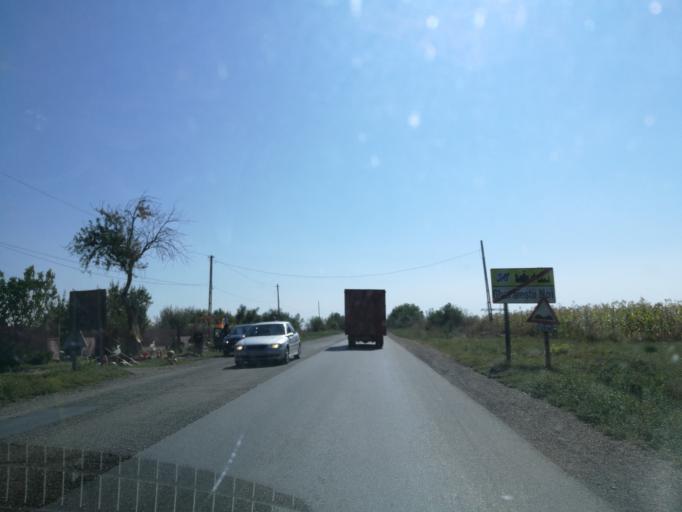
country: RO
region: Neamt
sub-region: Comuna Botesti
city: Barticesti
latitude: 47.0499
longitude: 26.7981
